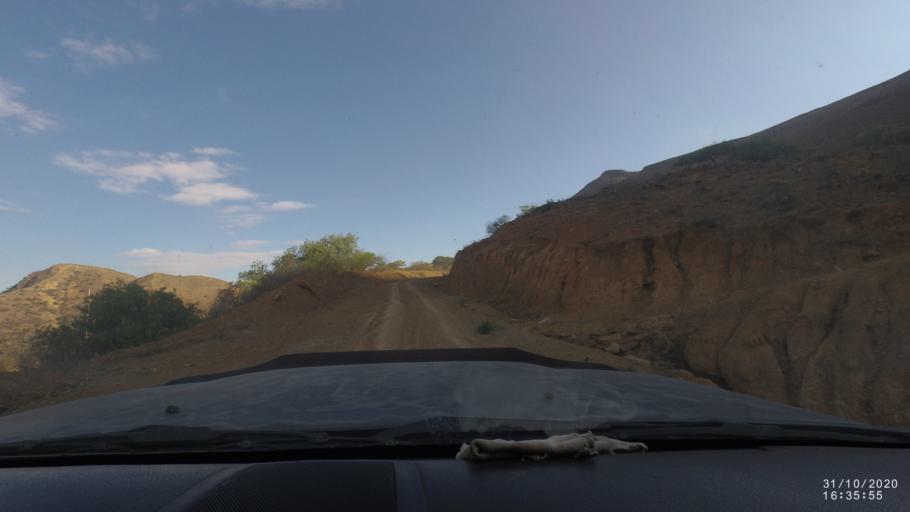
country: BO
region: Chuquisaca
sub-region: Provincia Zudanez
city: Mojocoya
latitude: -18.4562
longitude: -64.5826
